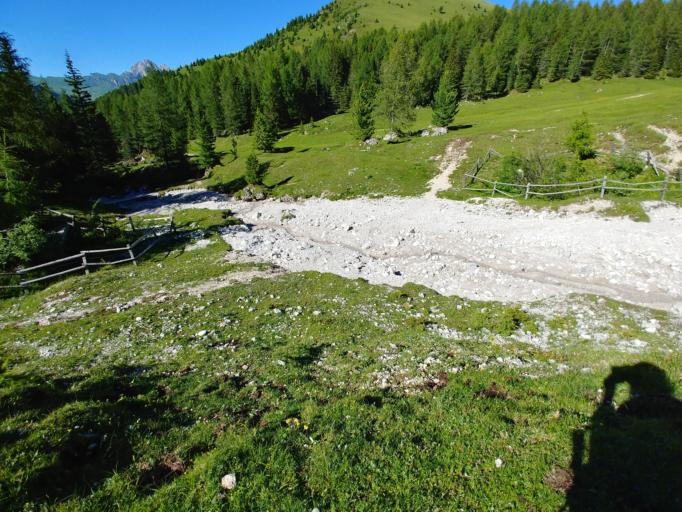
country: IT
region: Trentino-Alto Adige
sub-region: Bolzano
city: Santa Cristina Valgardena
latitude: 46.5323
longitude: 11.7378
